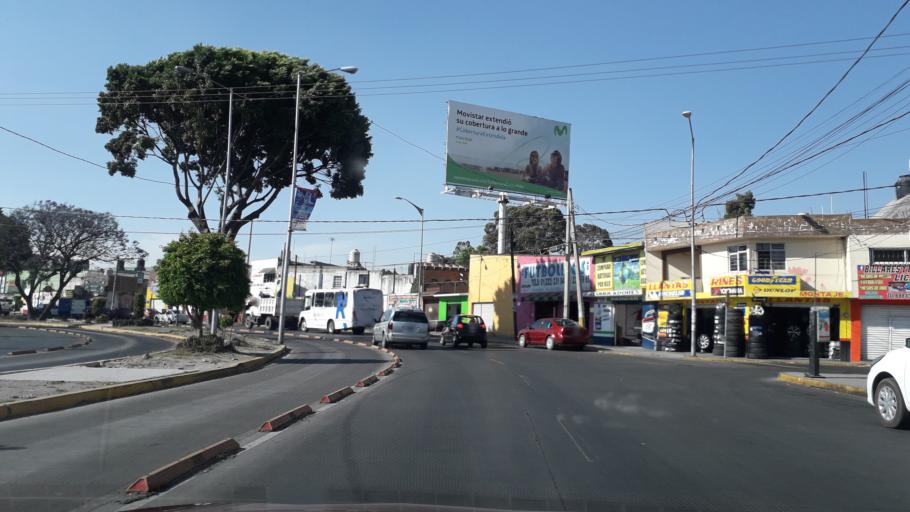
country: MX
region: Puebla
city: Puebla
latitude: 19.0656
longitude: -98.1907
